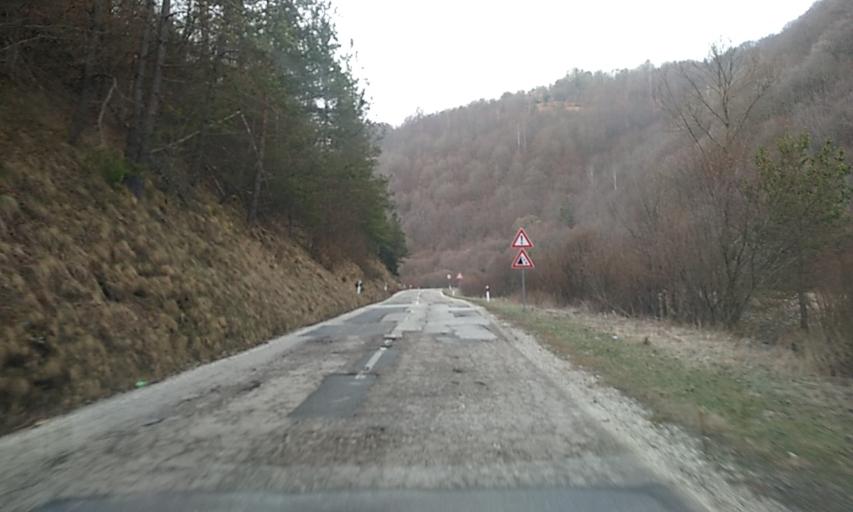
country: RS
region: Central Serbia
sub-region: Pcinjski Okrug
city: Bosilegrad
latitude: 42.6040
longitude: 22.4015
